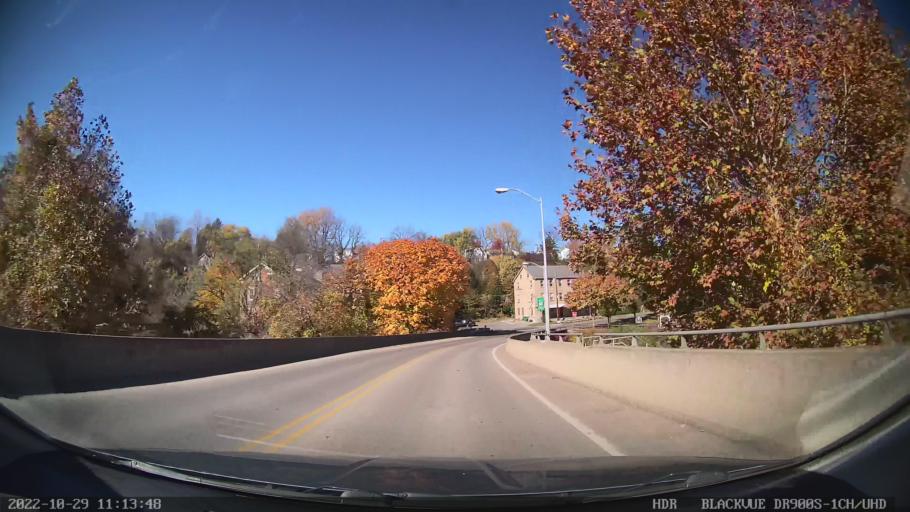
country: US
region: Pennsylvania
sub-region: Northampton County
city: Freemansburg
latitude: 40.6224
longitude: -75.3346
